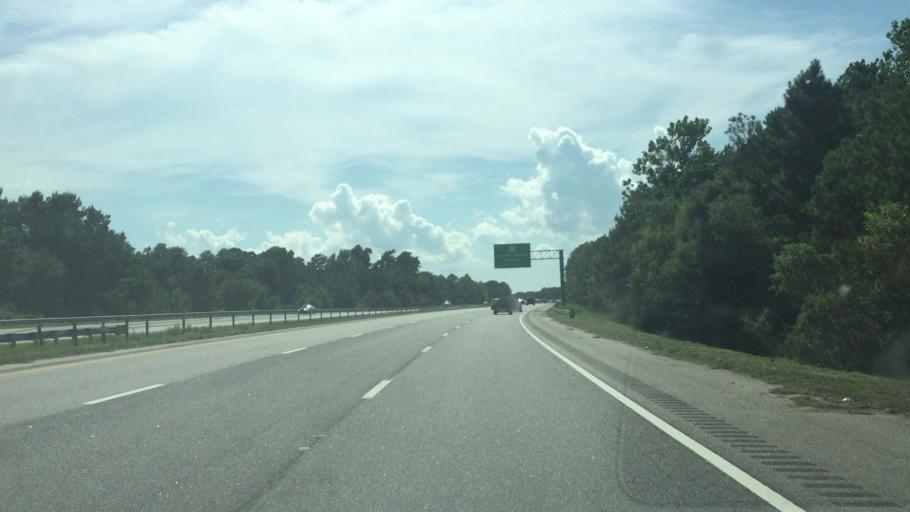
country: US
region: South Carolina
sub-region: Horry County
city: North Myrtle Beach
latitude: 33.8138
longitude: -78.7495
